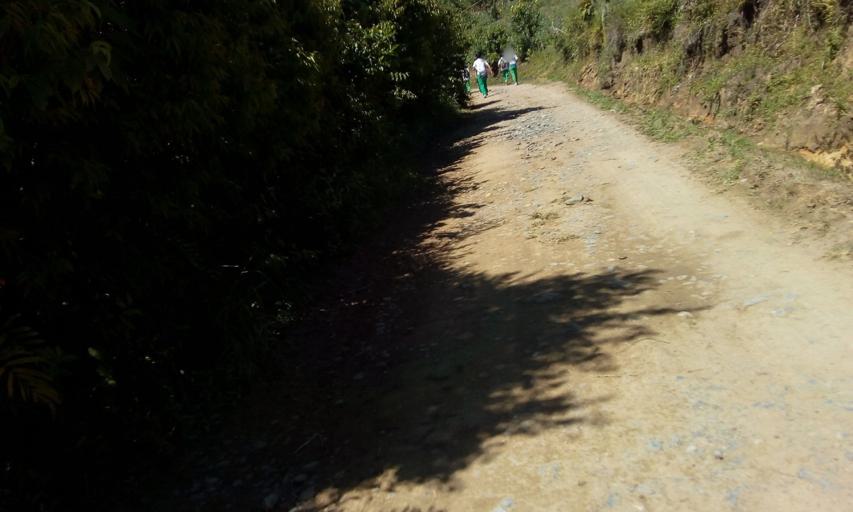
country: CO
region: Santander
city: Guepsa
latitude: 6.0065
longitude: -73.5484
